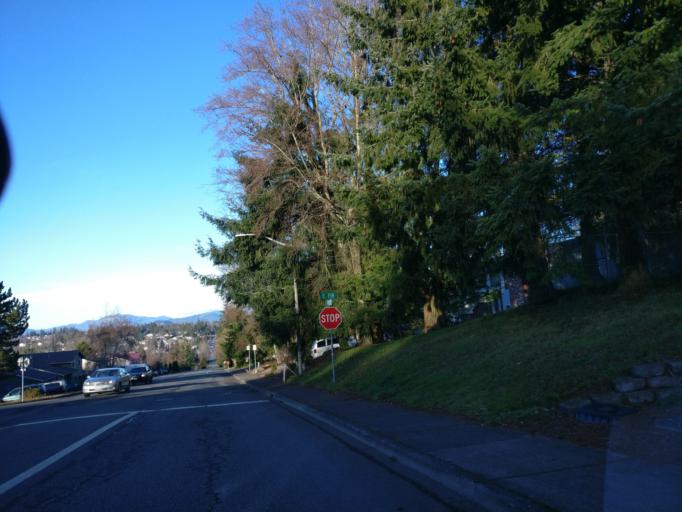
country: US
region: Washington
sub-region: Skagit County
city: Mount Vernon
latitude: 48.4280
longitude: -122.2918
